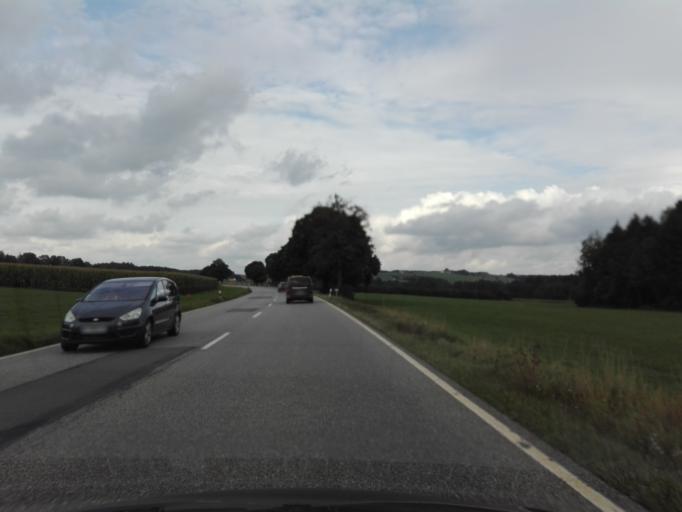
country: DE
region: Bavaria
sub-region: Upper Bavaria
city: Ramsau
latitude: 48.1819
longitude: 12.2560
